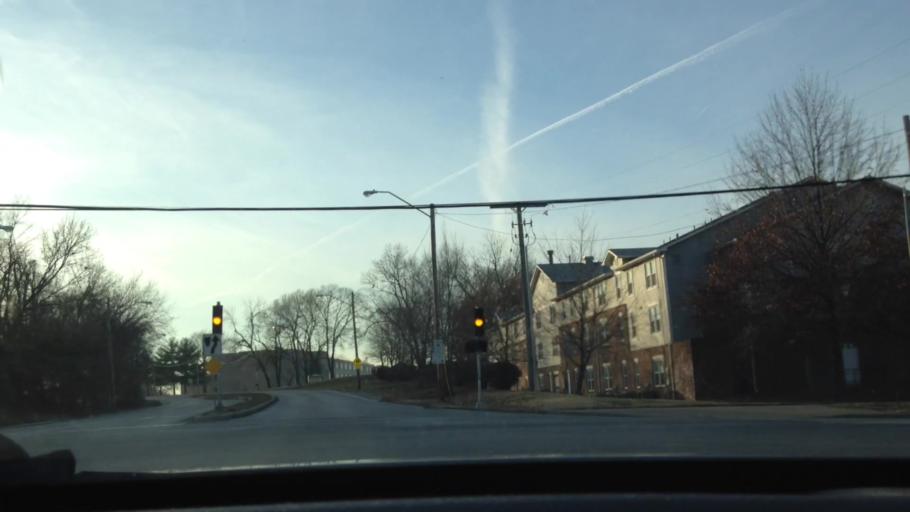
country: US
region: Missouri
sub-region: Clay County
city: Claycomo
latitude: 39.1671
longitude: -94.5213
